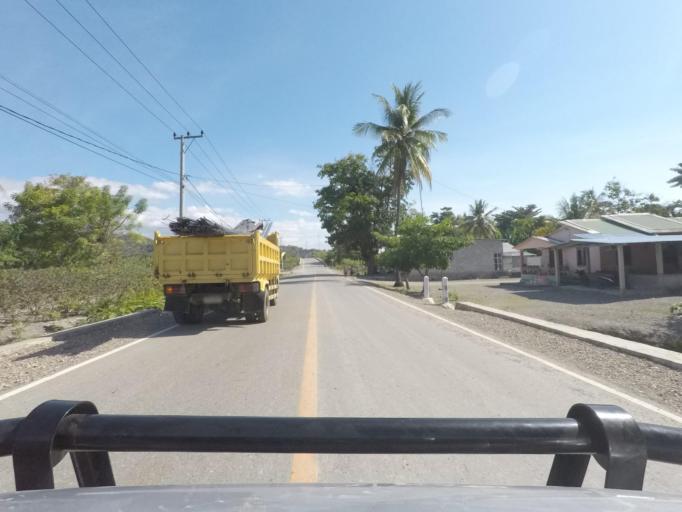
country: ID
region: East Nusa Tenggara
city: Atambua
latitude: -8.9441
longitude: 124.9766
